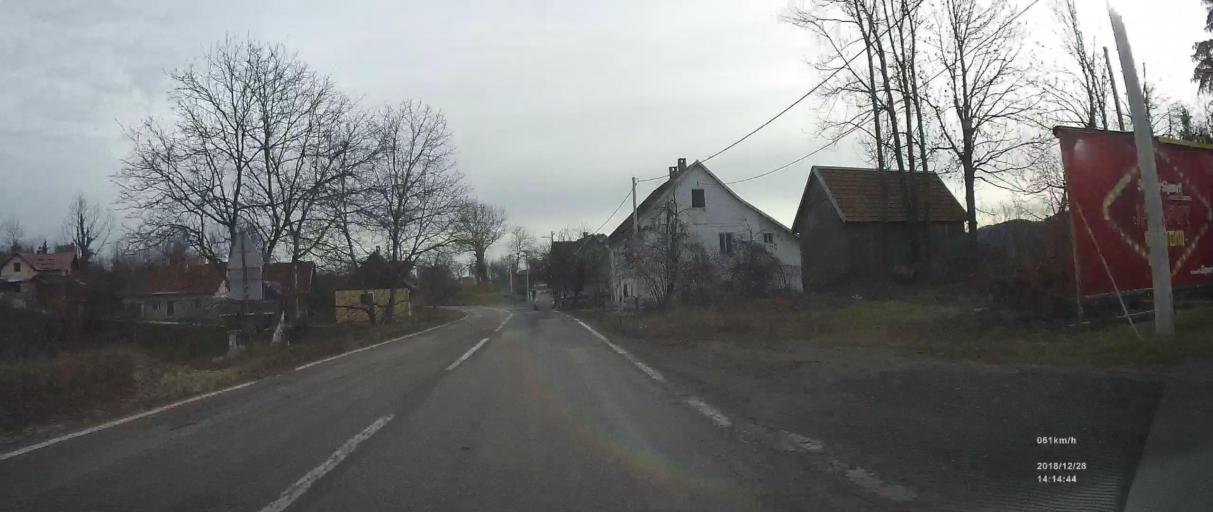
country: HR
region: Primorsko-Goranska
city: Vrbovsko
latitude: 45.4298
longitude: 15.0218
